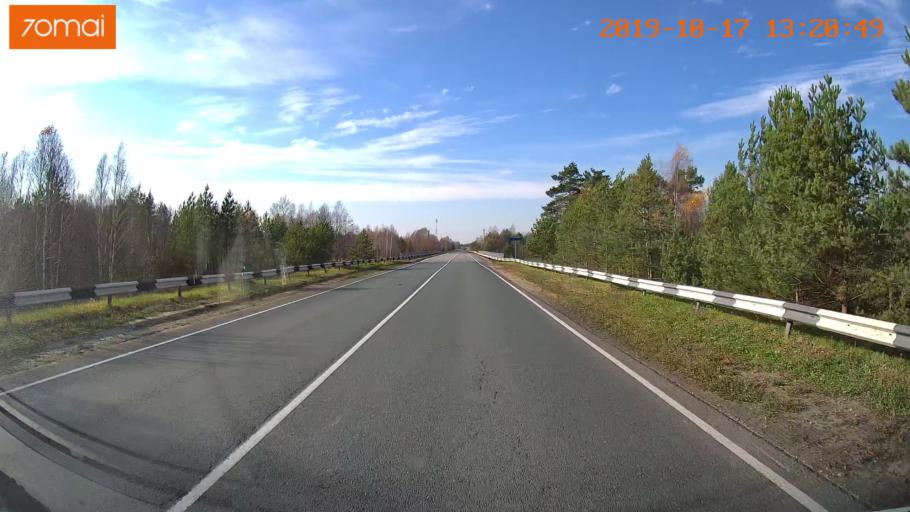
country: RU
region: Rjazan
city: Gus'-Zheleznyy
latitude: 55.0786
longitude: 41.0419
